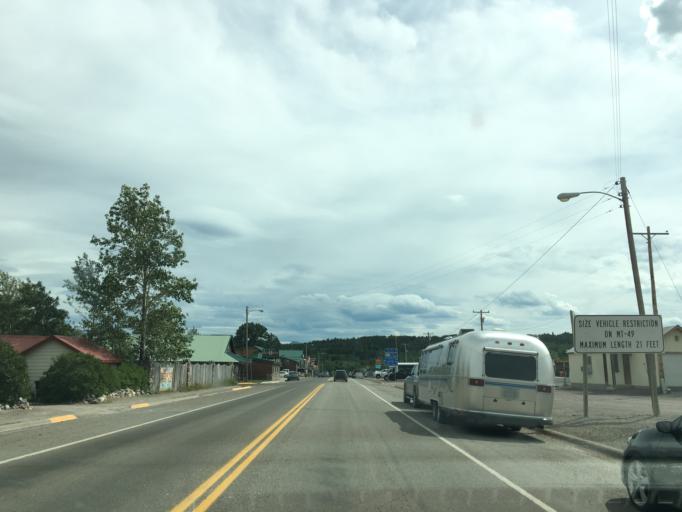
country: US
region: Montana
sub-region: Glacier County
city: South Browning
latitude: 48.4437
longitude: -113.2180
